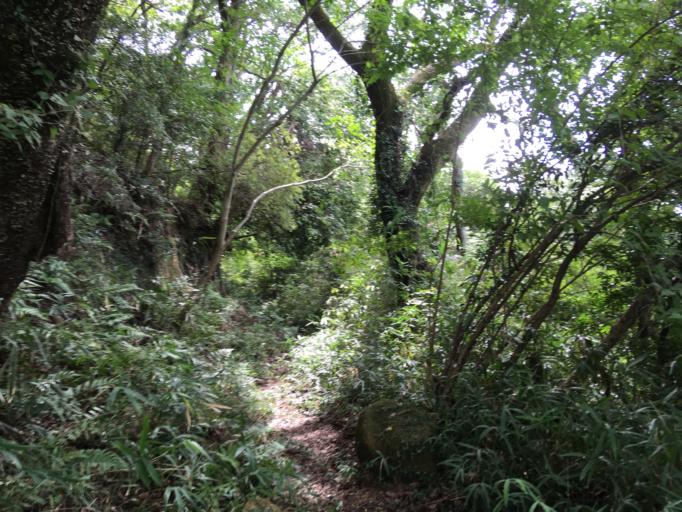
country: JP
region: Nara
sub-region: Ikoma-shi
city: Ikoma
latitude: 34.7014
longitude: 135.6664
